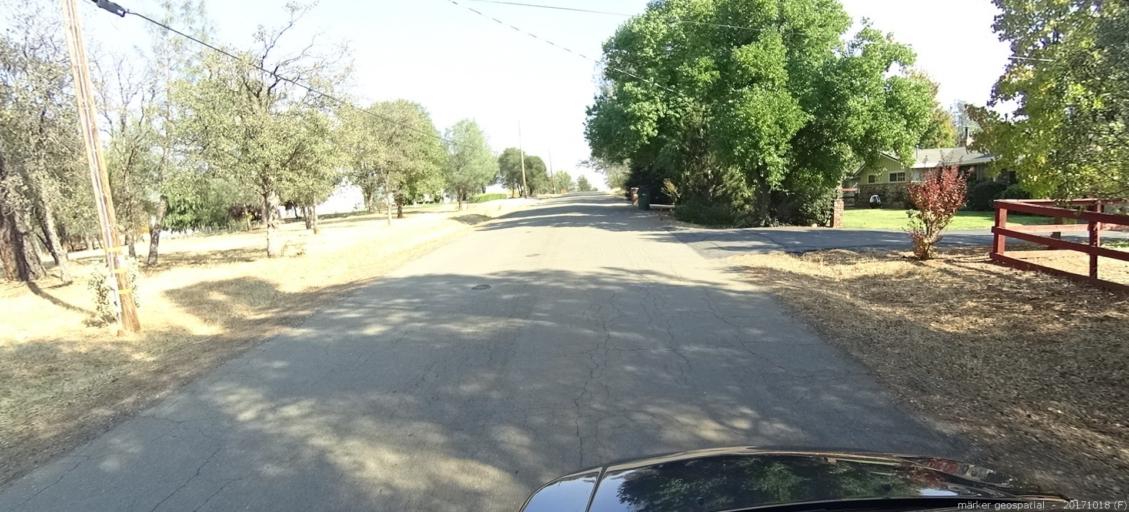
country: US
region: California
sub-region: Shasta County
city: Palo Cedro
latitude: 40.5529
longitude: -122.2789
